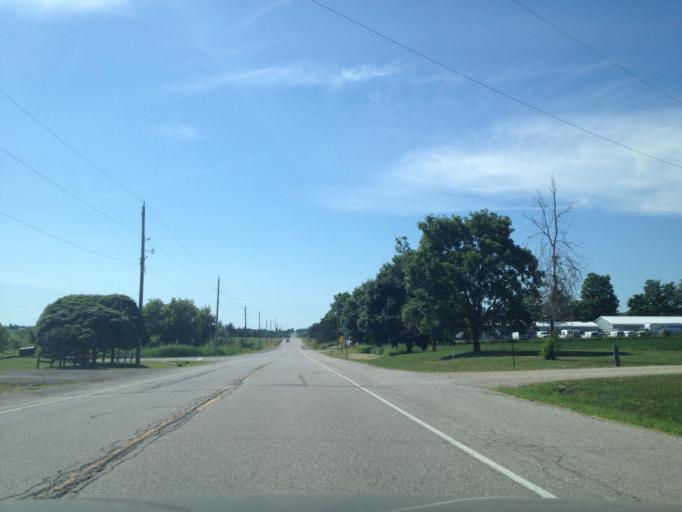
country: CA
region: Ontario
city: Stratford
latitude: 43.4781
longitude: -80.8203
